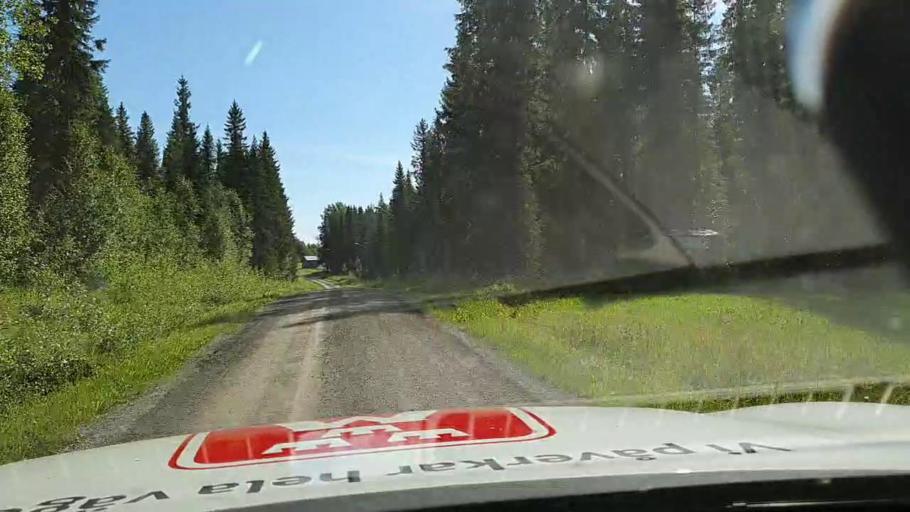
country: SE
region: Jaemtland
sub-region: Stroemsunds Kommun
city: Stroemsund
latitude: 63.7727
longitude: 15.3235
